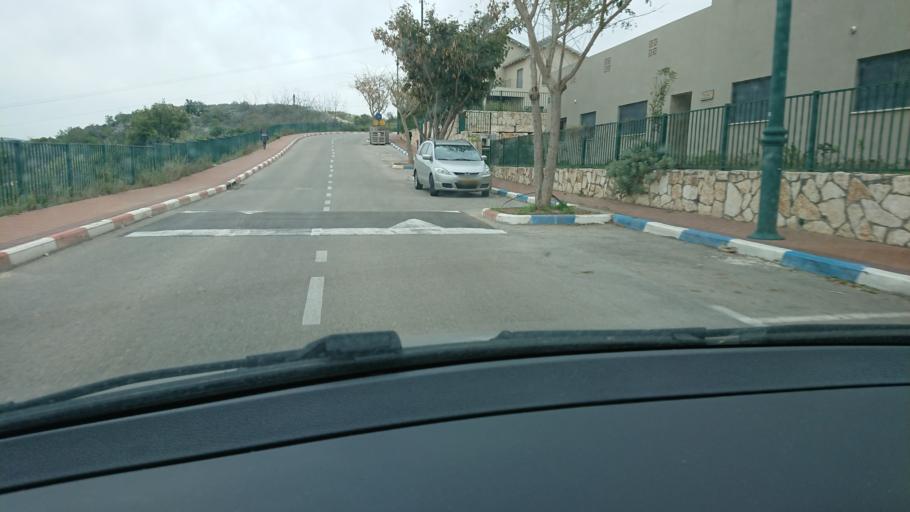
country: PS
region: West Bank
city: Rafat
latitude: 32.0653
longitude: 35.0557
